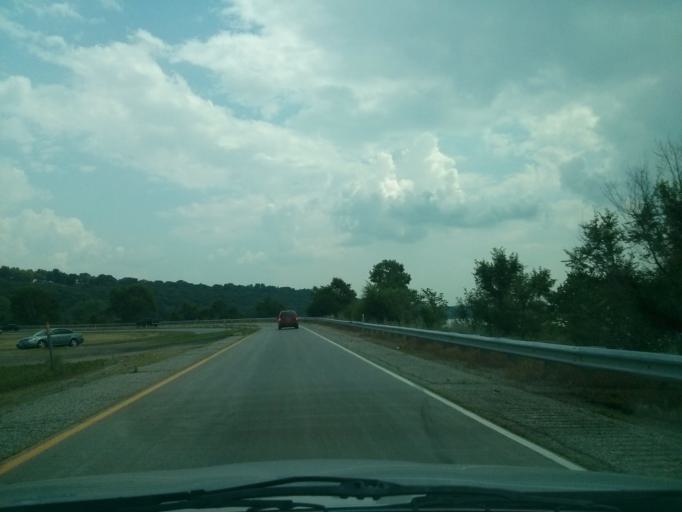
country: US
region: Minnesota
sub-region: Washington County
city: Lakeland
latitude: 44.9620
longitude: -92.7549
